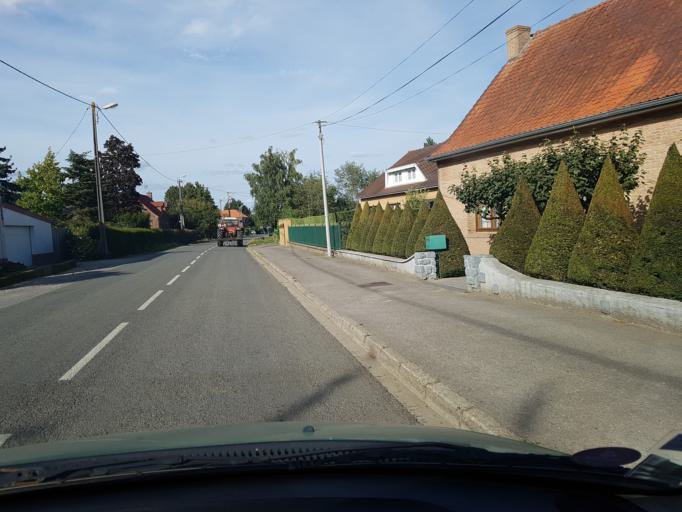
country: FR
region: Nord-Pas-de-Calais
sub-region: Departement du Pas-de-Calais
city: Hinges
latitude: 50.5898
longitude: 2.6316
